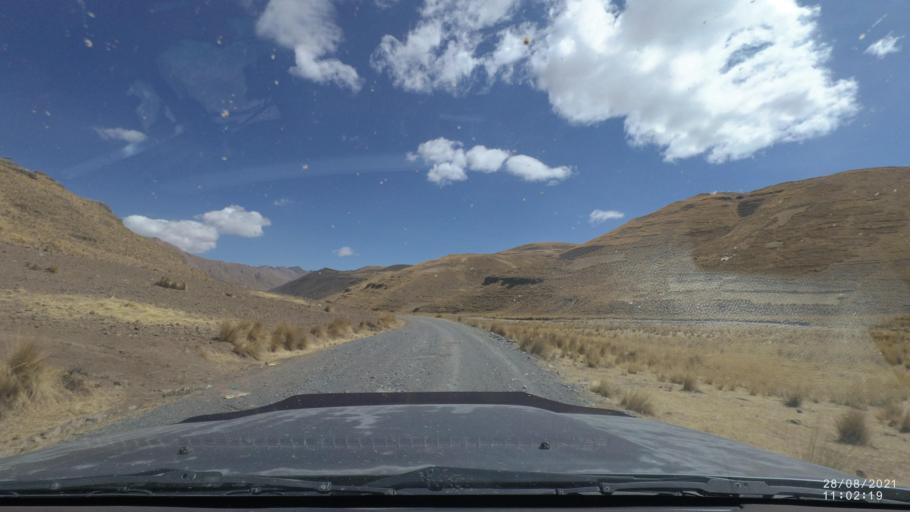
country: BO
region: Cochabamba
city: Cochabamba
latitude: -17.1780
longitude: -66.2715
